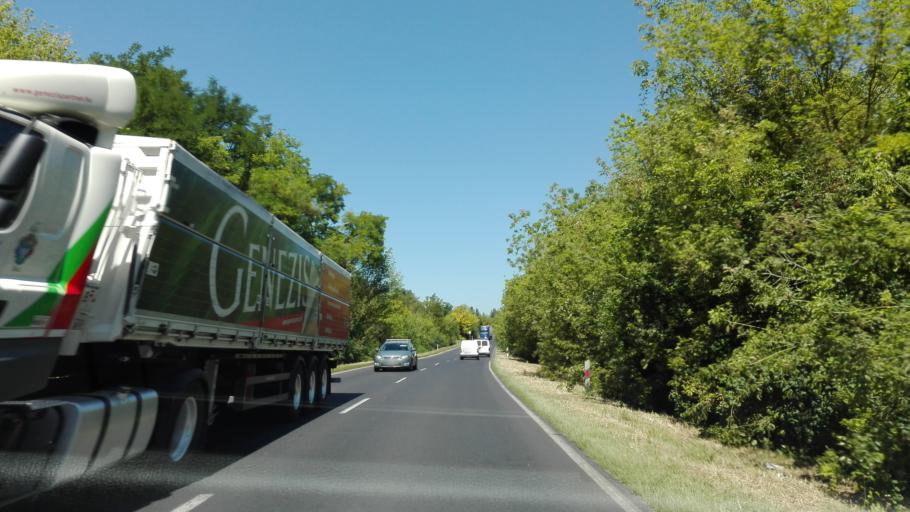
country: HU
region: Fejer
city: Mezoszilas
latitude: 46.7932
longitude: 18.4955
